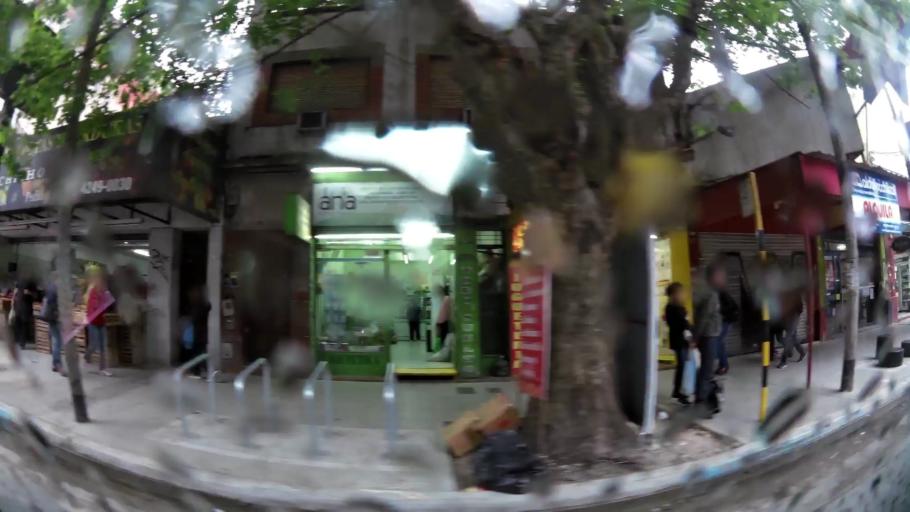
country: AR
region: Buenos Aires
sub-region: Partido de Lanus
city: Lanus
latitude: -34.7067
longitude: -58.3922
